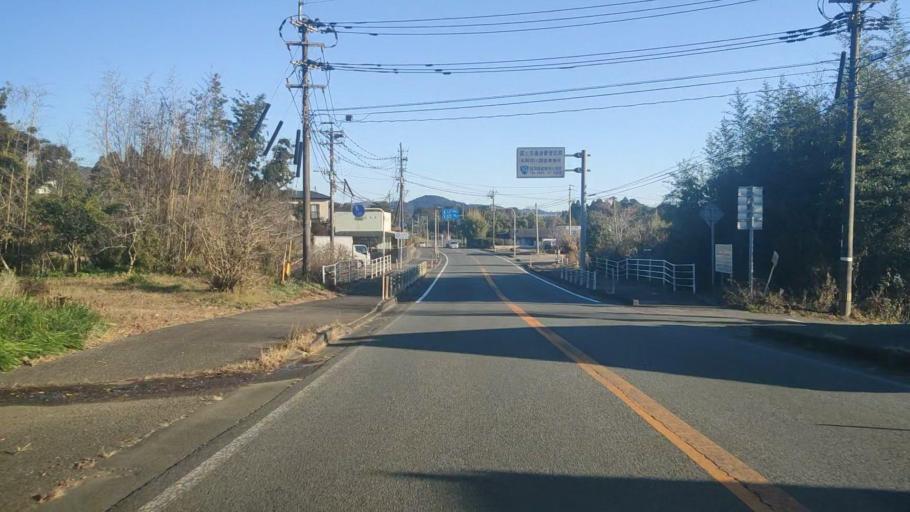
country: JP
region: Miyazaki
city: Takanabe
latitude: 32.3063
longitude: 131.5832
